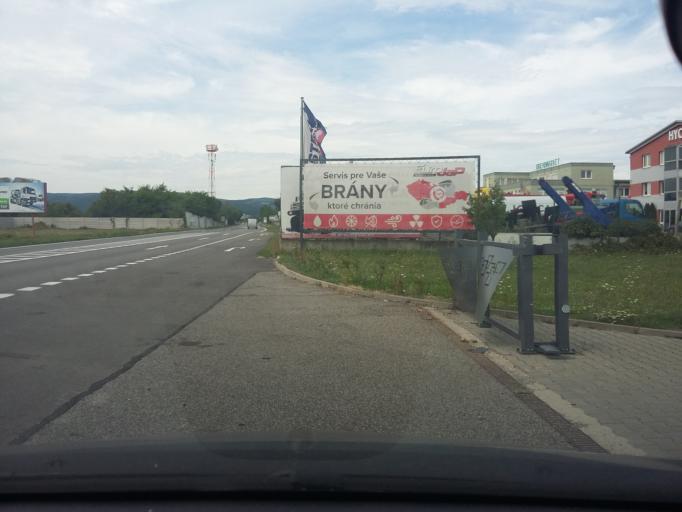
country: SK
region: Bratislavsky
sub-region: Okres Pezinok
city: Pezinok
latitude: 48.2854
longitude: 17.2850
